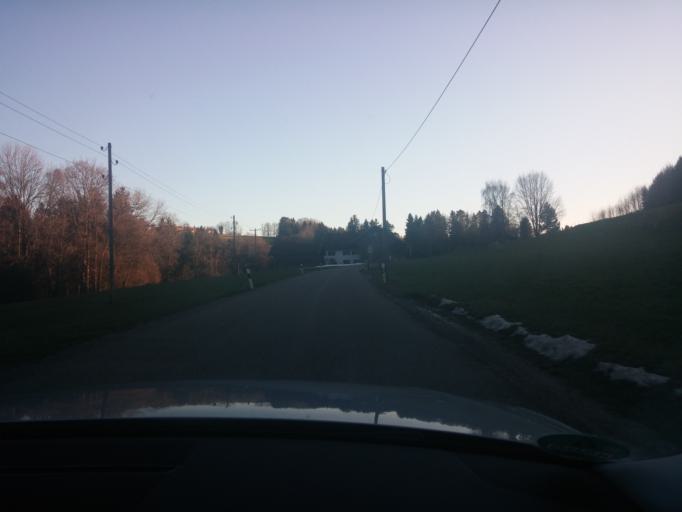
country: DE
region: Bavaria
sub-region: Swabia
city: Altusried
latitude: 47.8251
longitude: 10.1772
